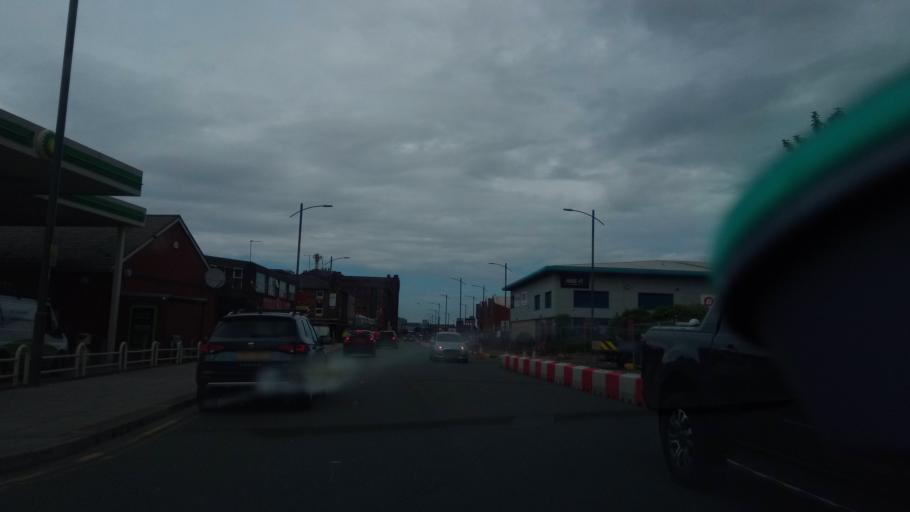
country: GB
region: England
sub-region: Liverpool
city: Liverpool
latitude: 53.4171
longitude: -2.9964
